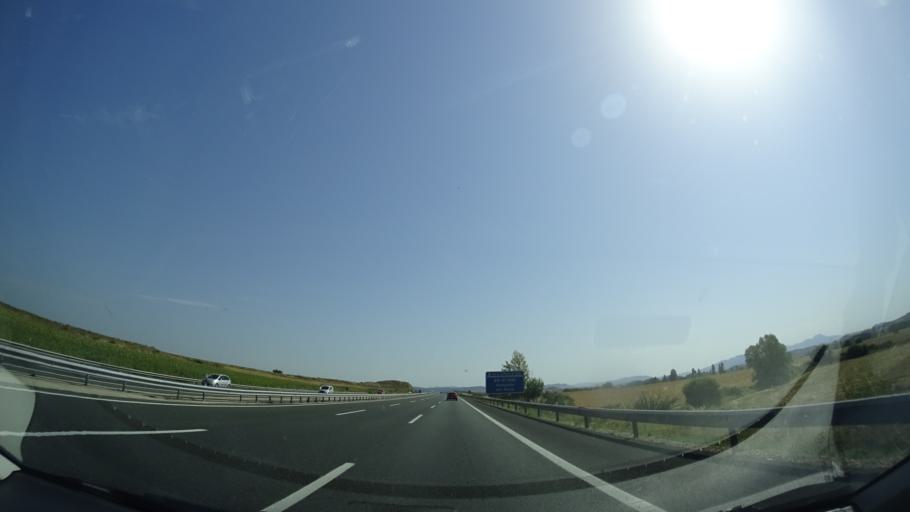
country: ES
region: Castille and Leon
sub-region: Provincia de Burgos
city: Bugedo
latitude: 42.6870
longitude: -2.9979
